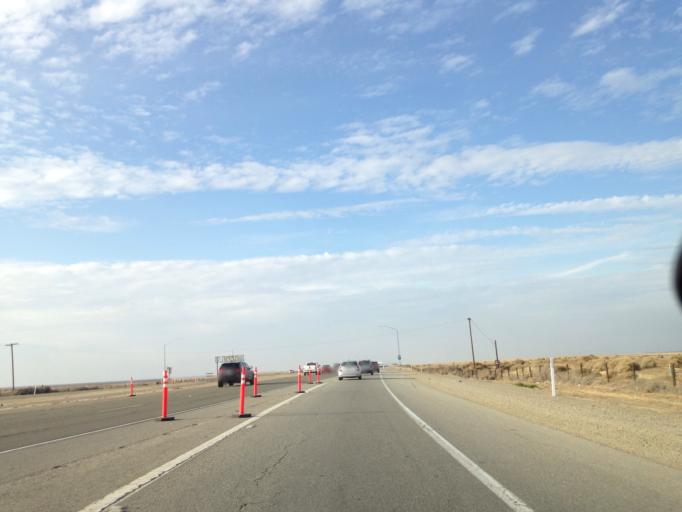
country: US
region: California
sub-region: Kern County
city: Lost Hills
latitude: 35.6188
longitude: -119.6548
